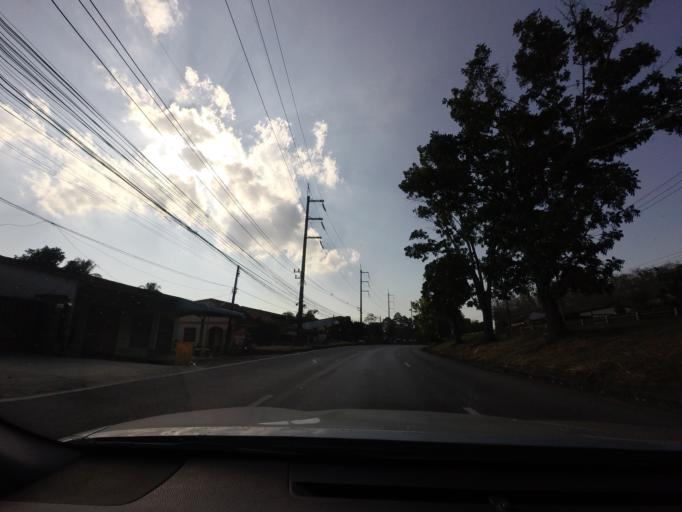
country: TH
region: Phangnga
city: Thai Mueang
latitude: 8.2703
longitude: 98.3187
